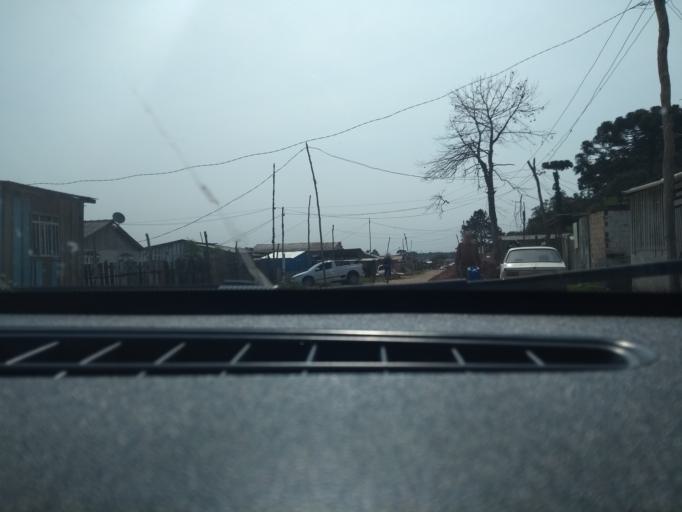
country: BR
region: Parana
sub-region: Araucaria
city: Araucaria
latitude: -25.6269
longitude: -49.3583
